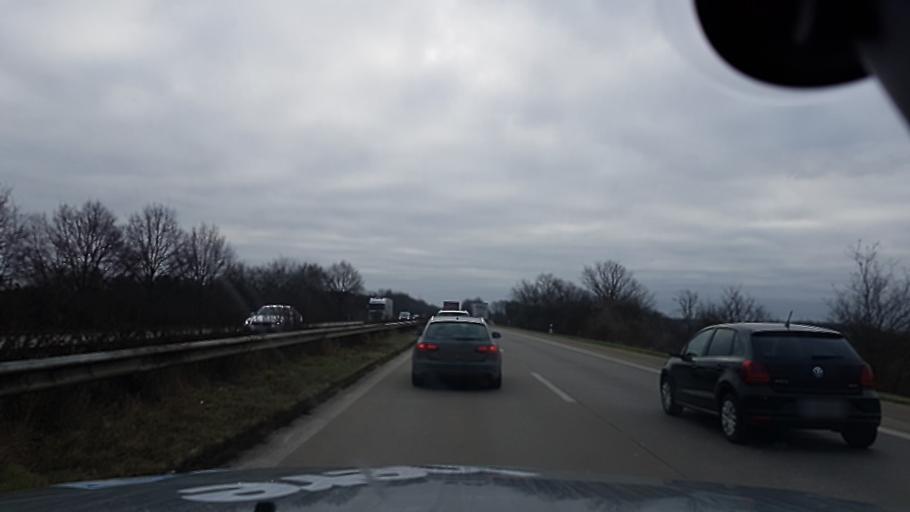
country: DE
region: Schleswig-Holstein
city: Ratekau
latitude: 53.9633
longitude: 10.7386
